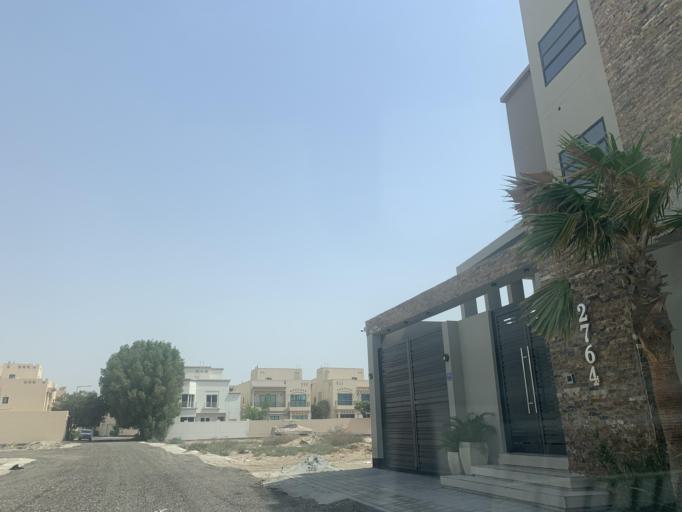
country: BH
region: Northern
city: Madinat `Isa
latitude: 26.1906
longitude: 50.4924
